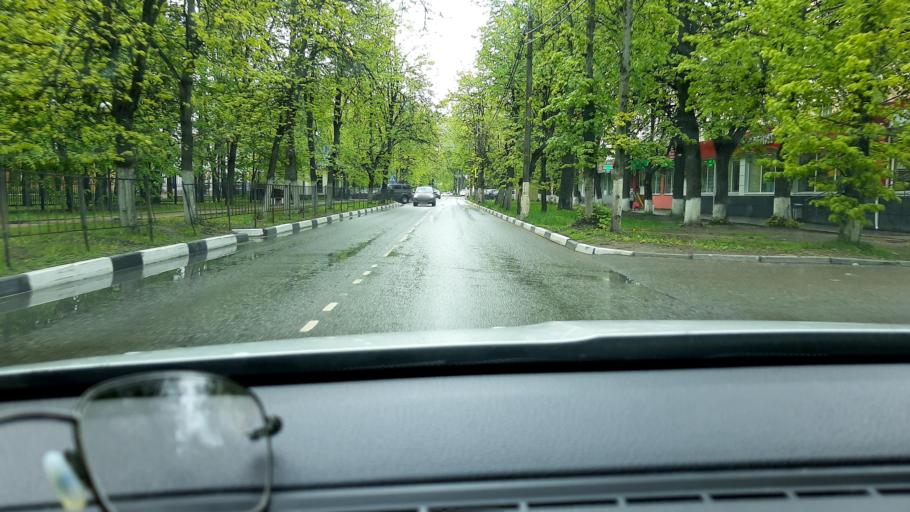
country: RU
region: Moskovskaya
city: Krasnogorsk
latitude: 55.8264
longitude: 37.3308
